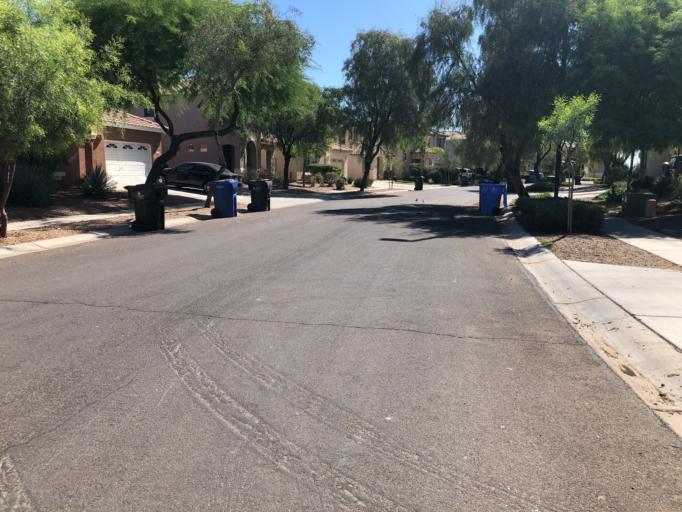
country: US
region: Arizona
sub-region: Maricopa County
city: Queen Creek
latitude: 33.2759
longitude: -111.7090
